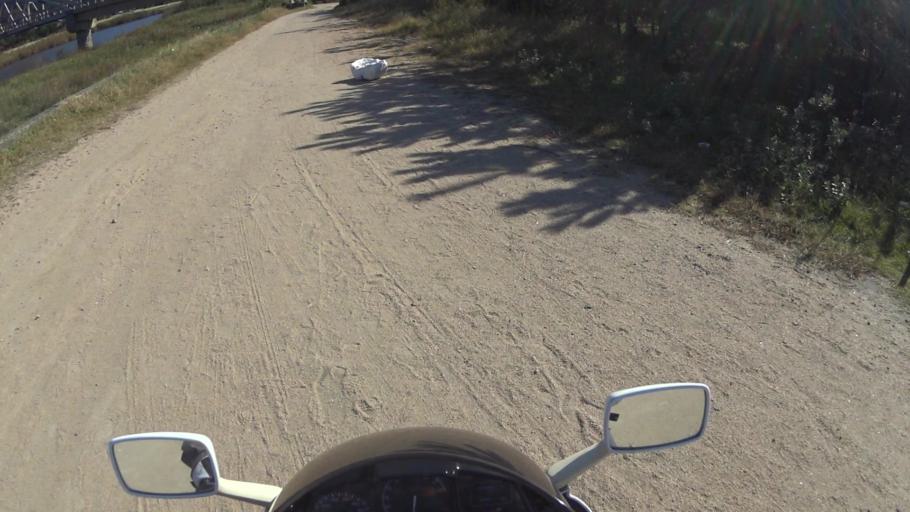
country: JP
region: Kyoto
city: Miyazu
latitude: 35.7426
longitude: 135.1059
